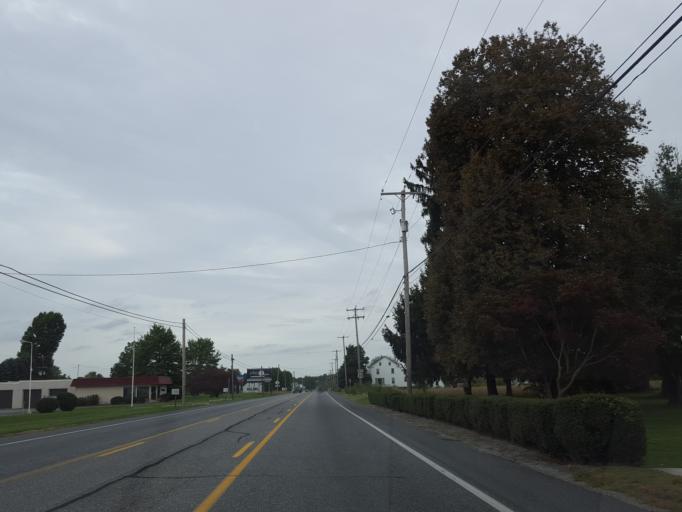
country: US
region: Pennsylvania
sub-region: York County
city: Spring Grove
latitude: 39.9223
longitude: -76.8891
